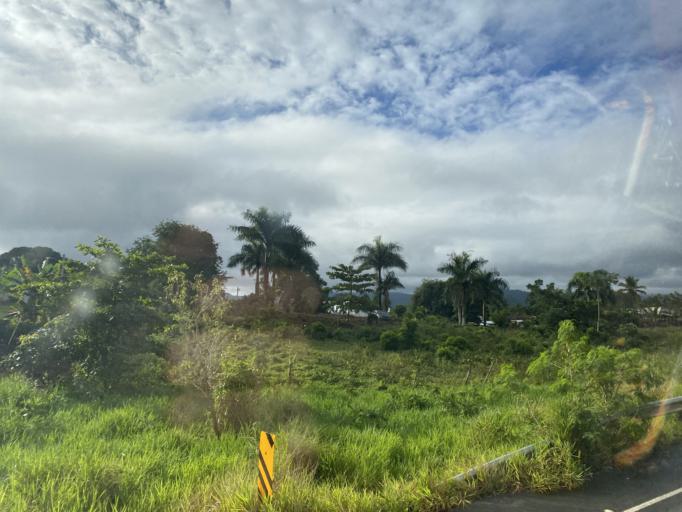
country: DO
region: El Seibo
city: Miches
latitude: 18.9611
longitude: -68.9828
